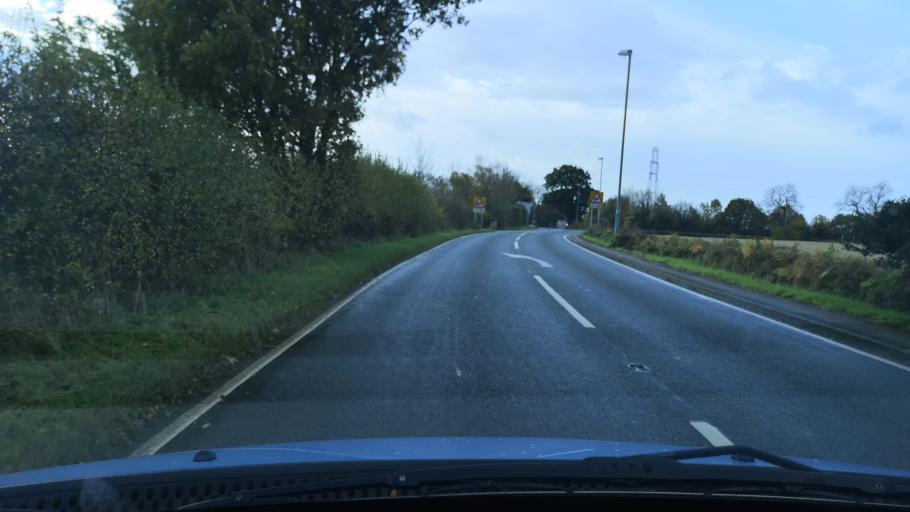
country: GB
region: England
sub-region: City and Borough of Wakefield
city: Ryhill
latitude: 53.6151
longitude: -1.4251
